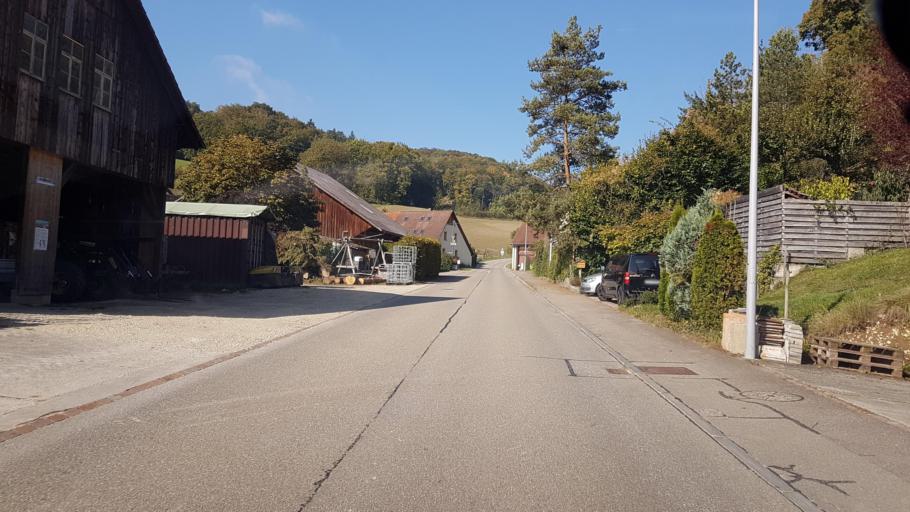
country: CH
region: Aargau
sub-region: Bezirk Laufenburg
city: Sulz
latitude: 47.5179
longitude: 8.1330
